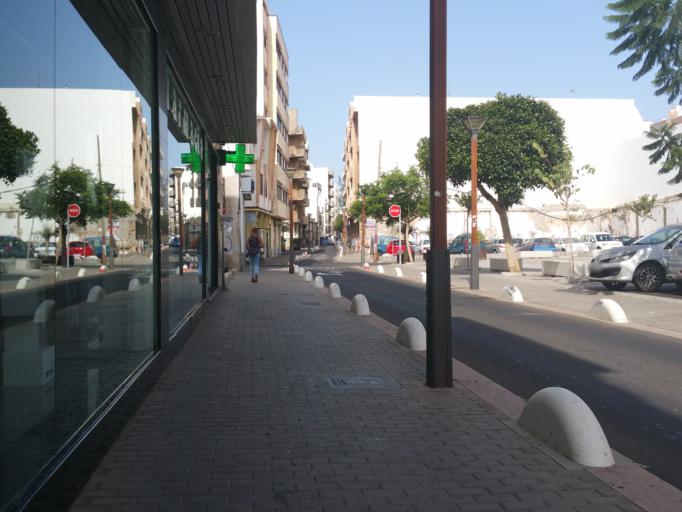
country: ES
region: Canary Islands
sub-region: Provincia de Las Palmas
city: Arrecife
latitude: 28.9587
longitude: -13.5509
